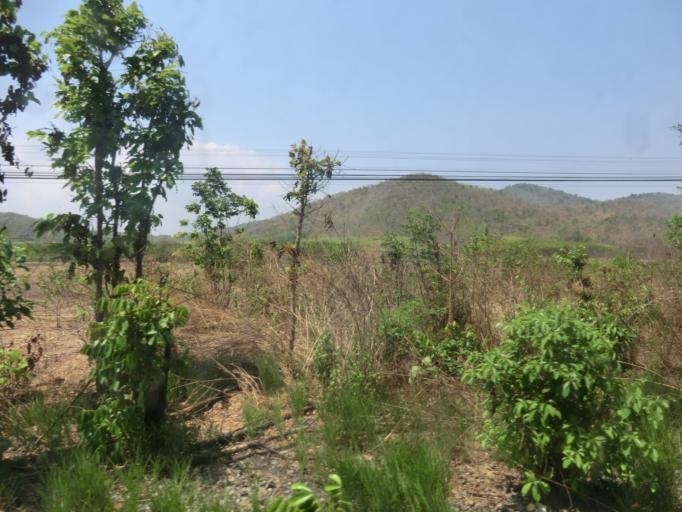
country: VN
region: Binh Thuan
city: Thuan Nam
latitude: 10.9107
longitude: 107.8440
